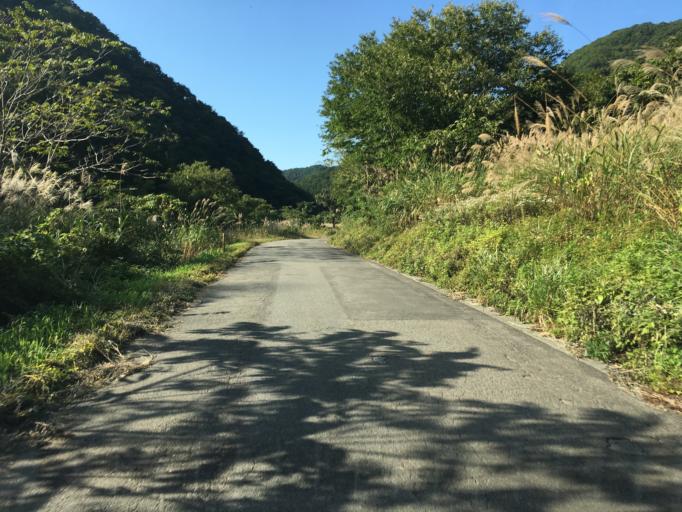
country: JP
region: Yamagata
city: Yonezawa
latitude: 37.8527
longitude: 140.1698
